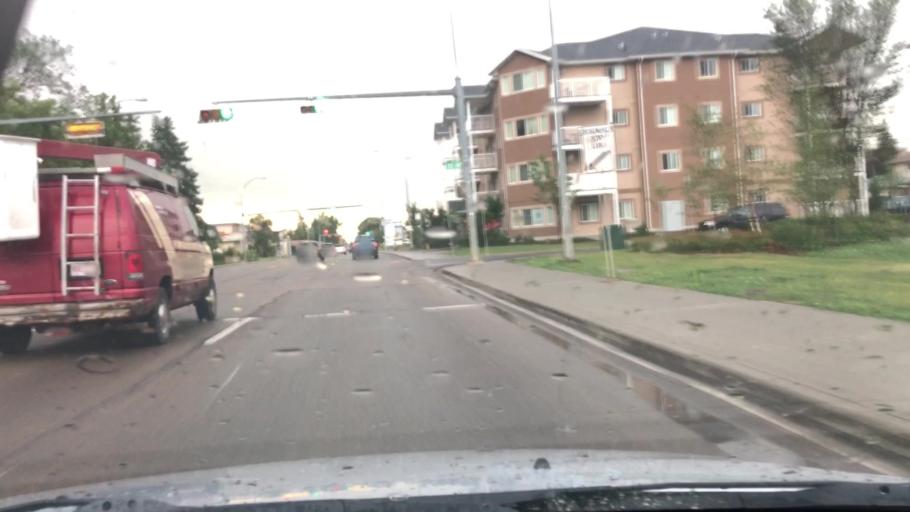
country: CA
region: Alberta
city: Edmonton
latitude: 53.5903
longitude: -113.5413
